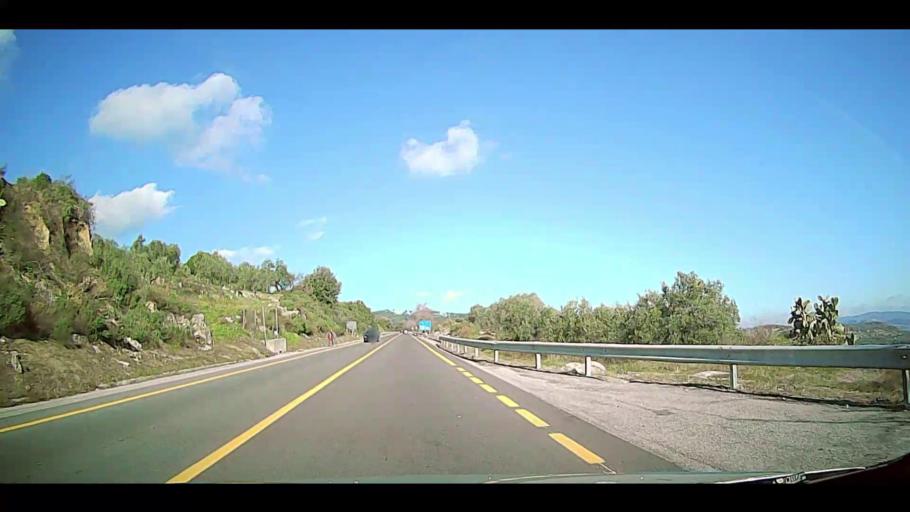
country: IT
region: Calabria
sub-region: Provincia di Crotone
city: Caccuri
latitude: 39.2280
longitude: 16.7952
